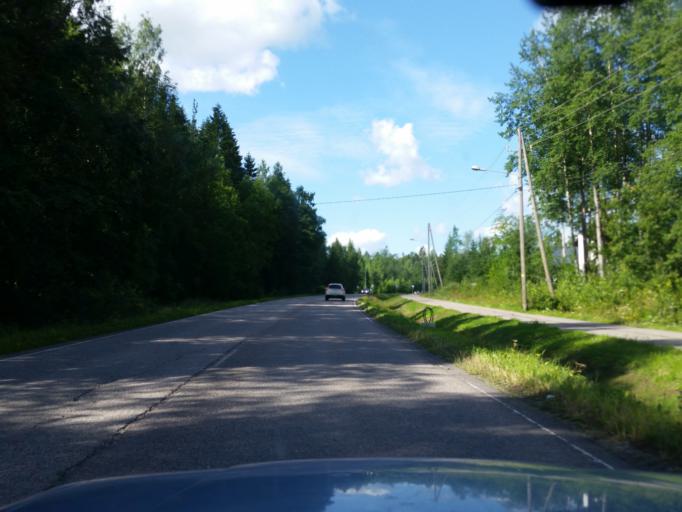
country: FI
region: Uusimaa
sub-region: Helsinki
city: Vihti
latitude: 60.3279
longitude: 24.3130
